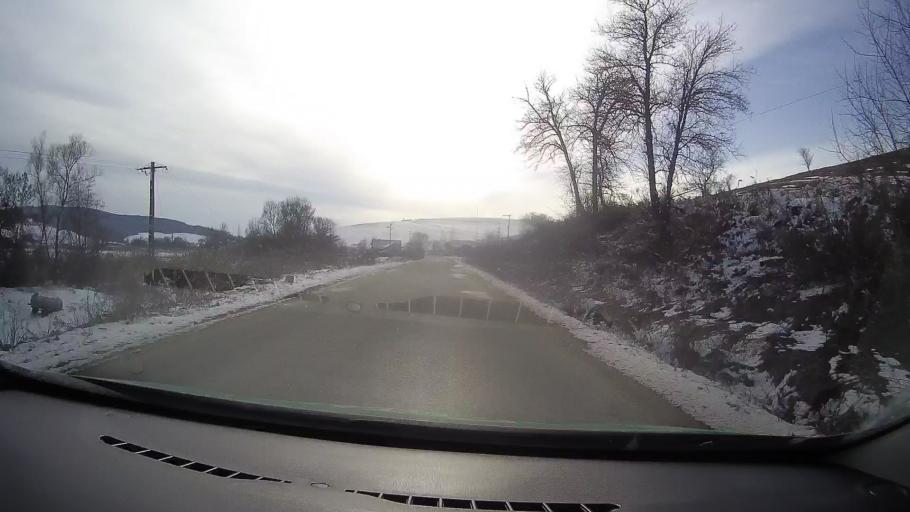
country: RO
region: Sibiu
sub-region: Oras Agnita
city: Ruja
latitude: 46.0038
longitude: 24.6750
